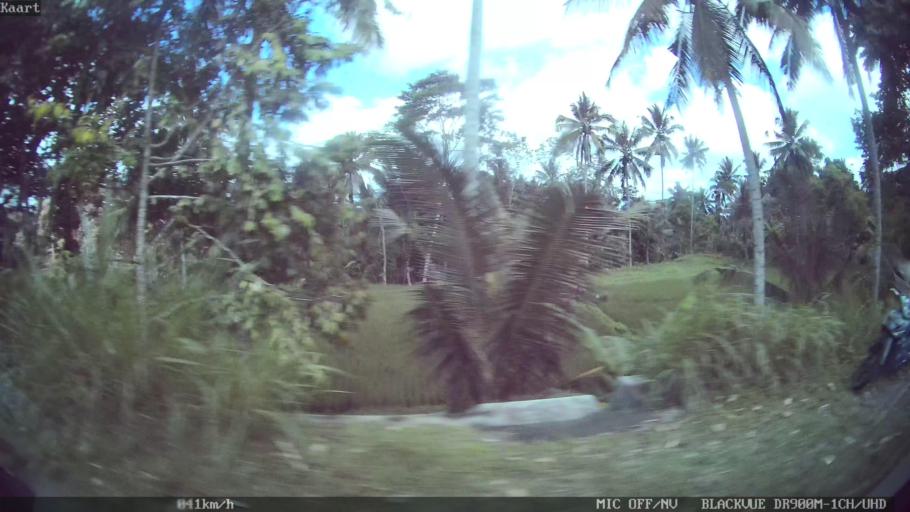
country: ID
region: Bali
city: Banjar Madangan Kaja
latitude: -8.4715
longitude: 115.3236
